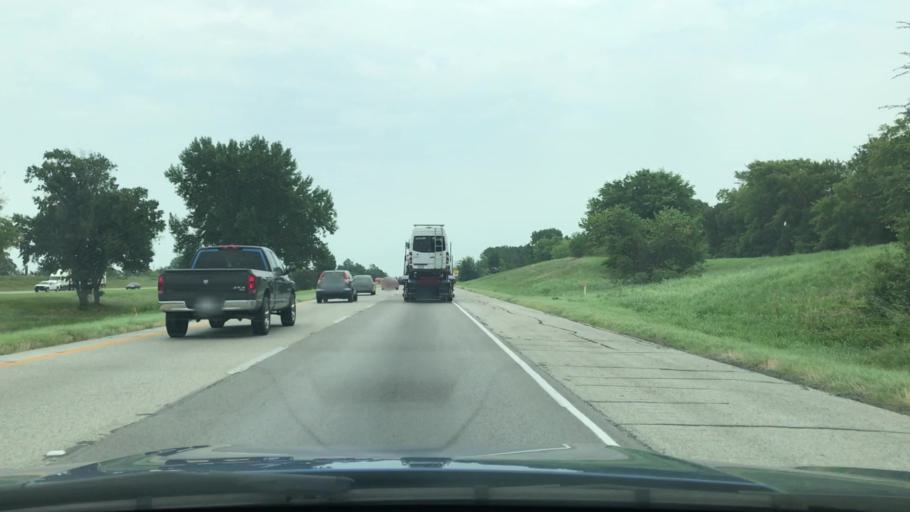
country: US
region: Texas
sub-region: Smith County
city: Hideaway
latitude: 32.4800
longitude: -95.4948
